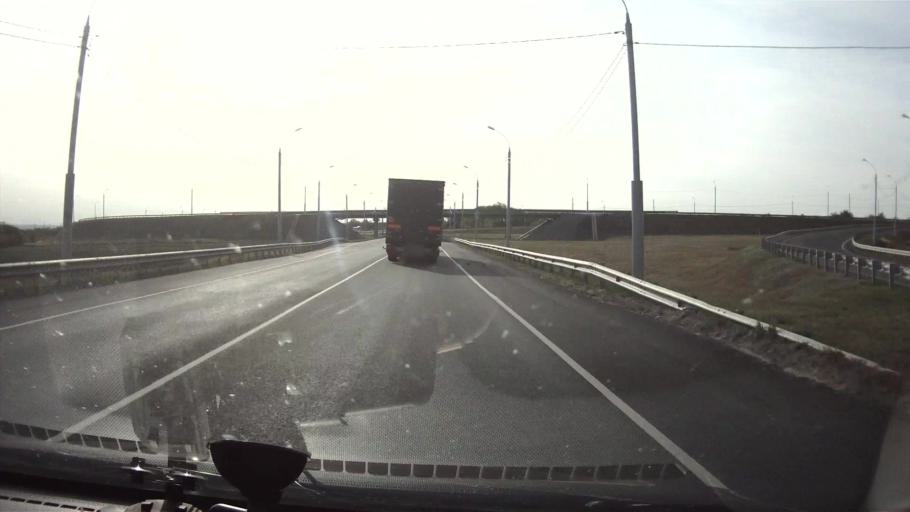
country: RU
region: Saratov
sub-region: Saratovskiy Rayon
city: Saratov
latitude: 51.7747
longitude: 46.0946
